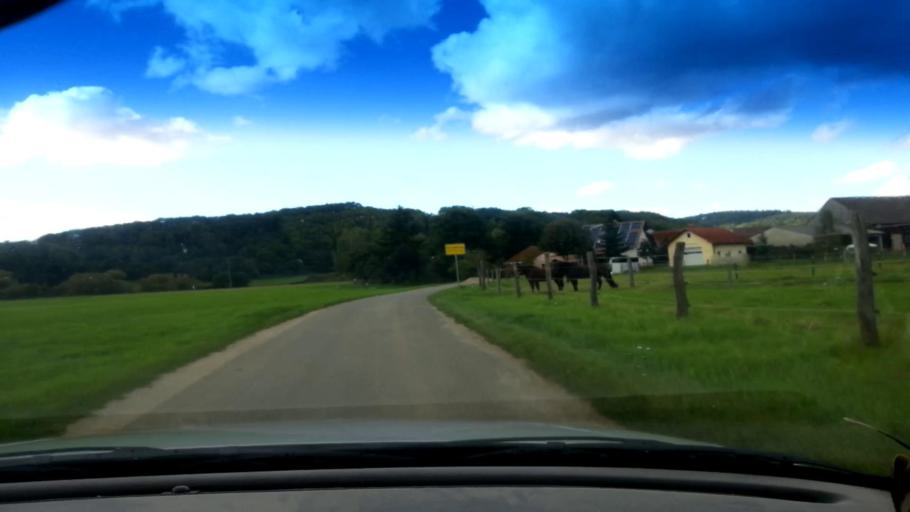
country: DE
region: Bavaria
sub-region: Upper Franconia
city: Ebensfeld
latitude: 50.0795
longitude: 10.9467
